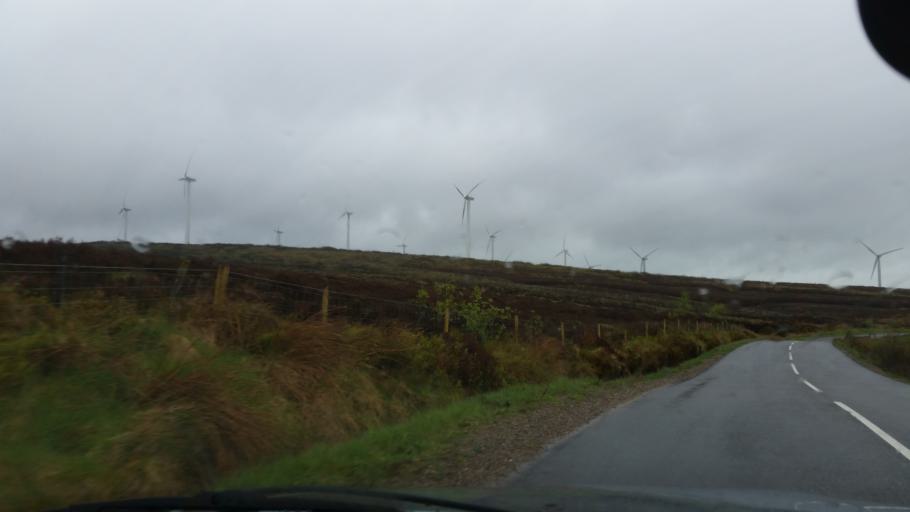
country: GB
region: Northern Ireland
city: Fintona
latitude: 54.4390
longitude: -7.3279
